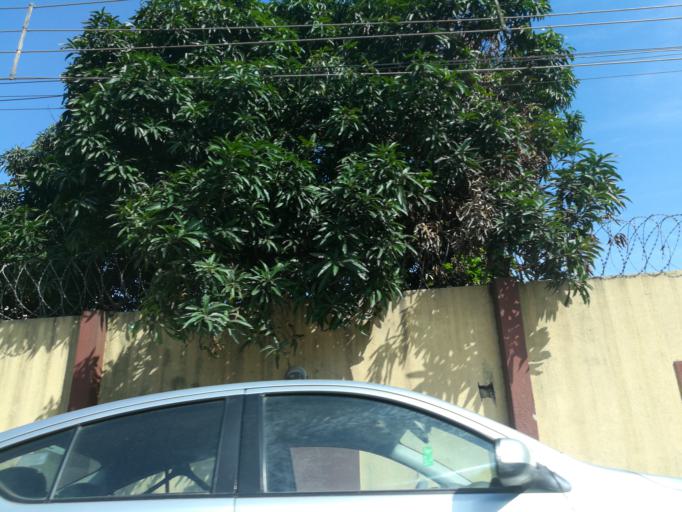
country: NG
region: Lagos
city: Ikeja
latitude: 6.6054
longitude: 3.3436
